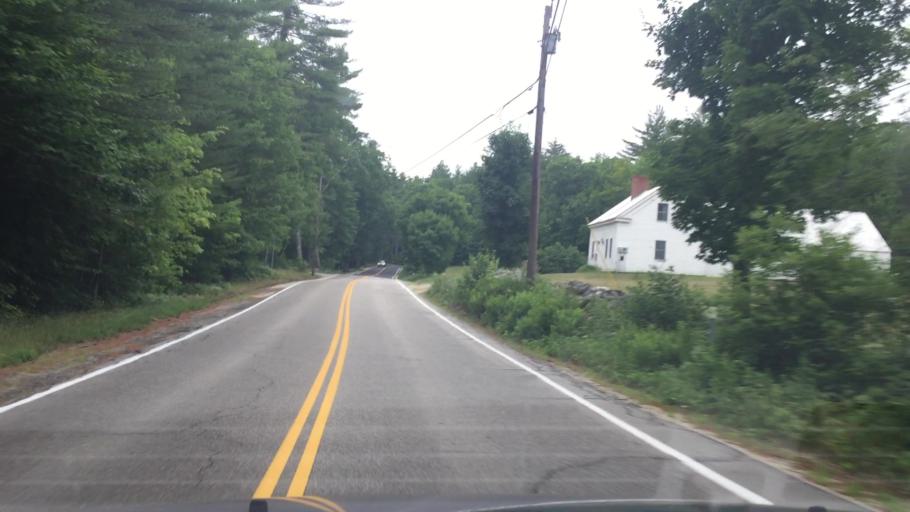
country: US
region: New Hampshire
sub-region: Carroll County
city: Madison
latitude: 43.8796
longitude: -71.0841
